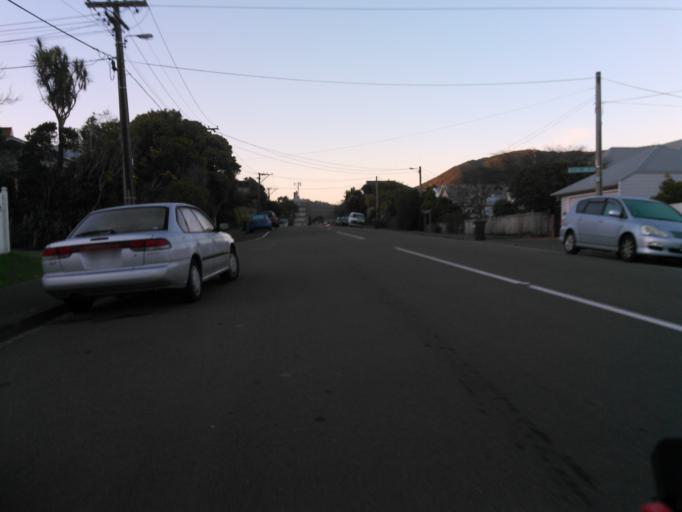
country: NZ
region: Wellington
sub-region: Wellington City
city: Kelburn
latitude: -41.2826
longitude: 174.7397
